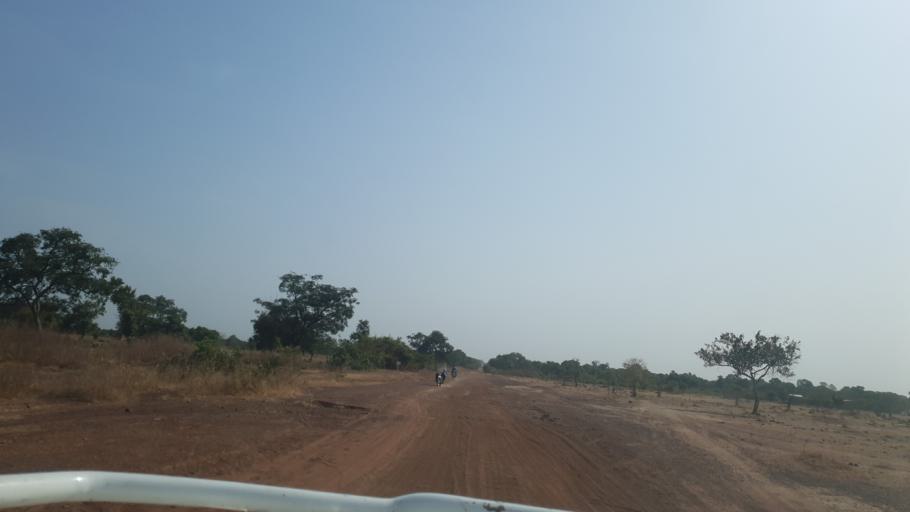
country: ML
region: Koulikoro
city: Dioila
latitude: 12.6681
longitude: -6.6886
